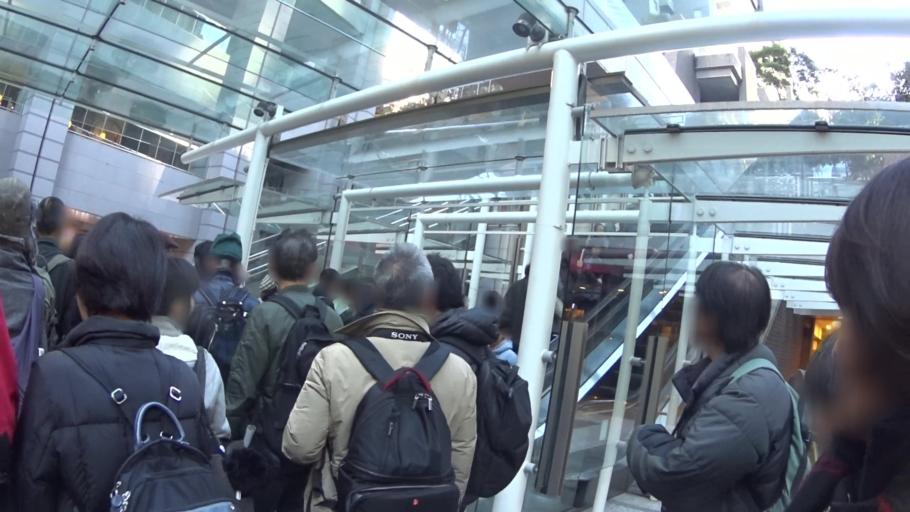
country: JP
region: Tokyo
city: Tokyo
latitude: 35.6655
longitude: 139.7402
